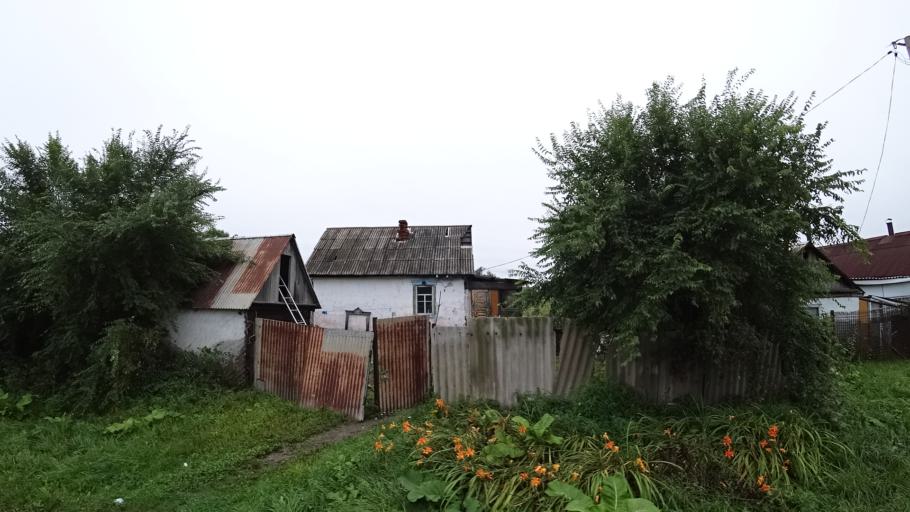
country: RU
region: Primorskiy
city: Monastyrishche
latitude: 44.2067
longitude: 132.4351
